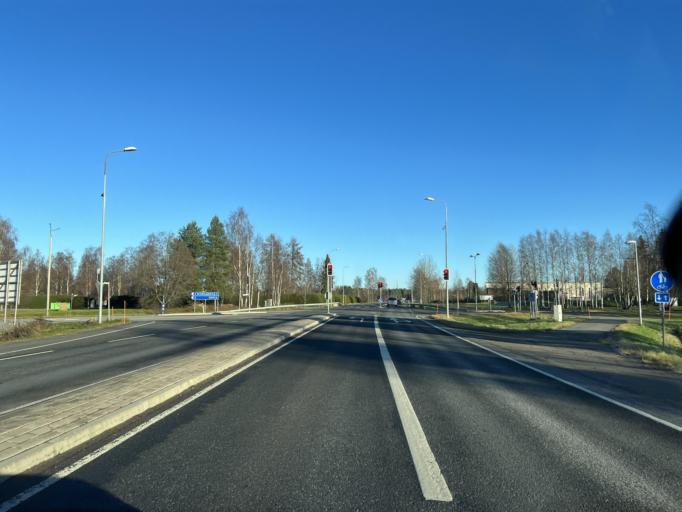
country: FI
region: Northern Ostrobothnia
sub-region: Ylivieska
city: Ylivieska
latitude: 64.0765
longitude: 24.5182
